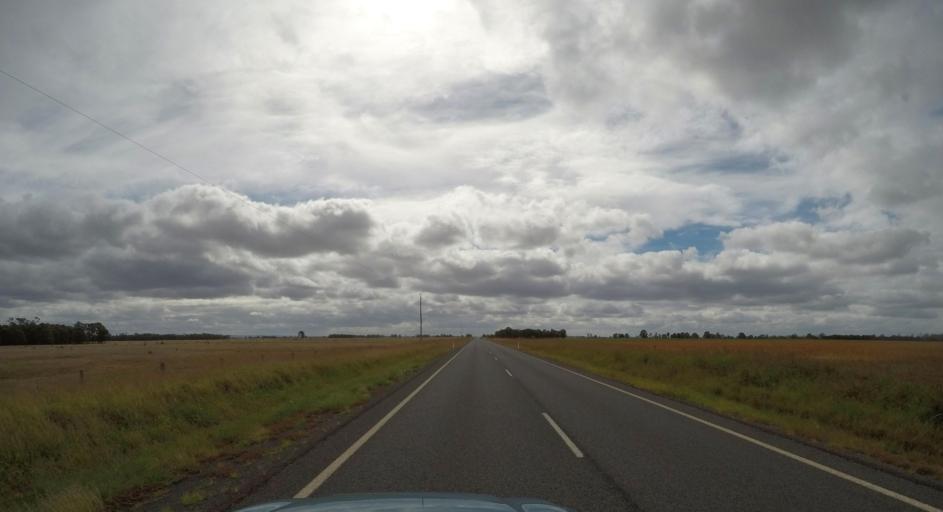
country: AU
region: Queensland
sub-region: South Burnett
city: Kingaroy
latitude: -26.3532
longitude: 151.2505
